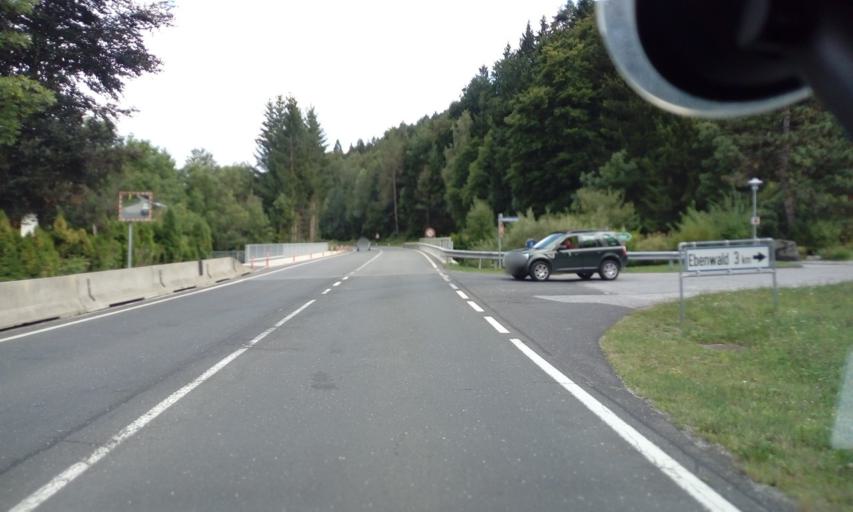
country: AT
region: Carinthia
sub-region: Politischer Bezirk Villach Land
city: Fresach
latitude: 46.6634
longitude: 13.7353
